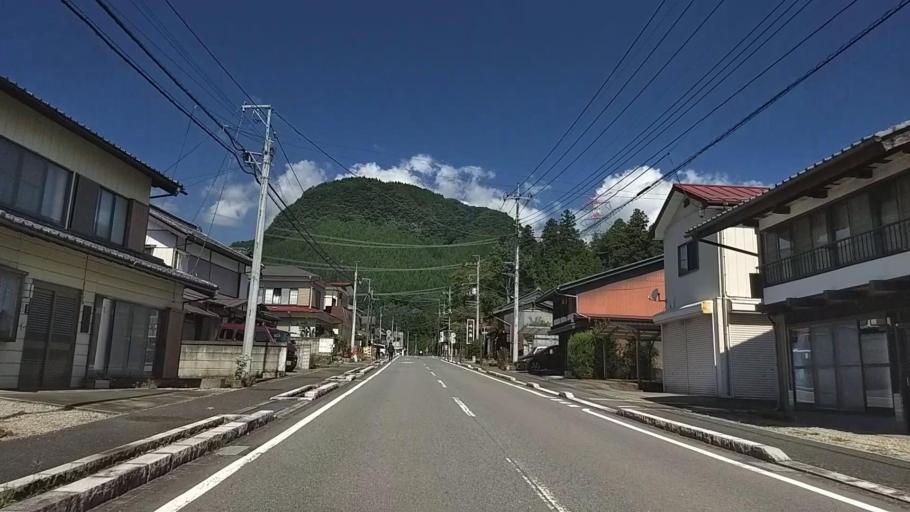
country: JP
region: Gunma
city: Annaka
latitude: 36.3507
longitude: 138.7165
